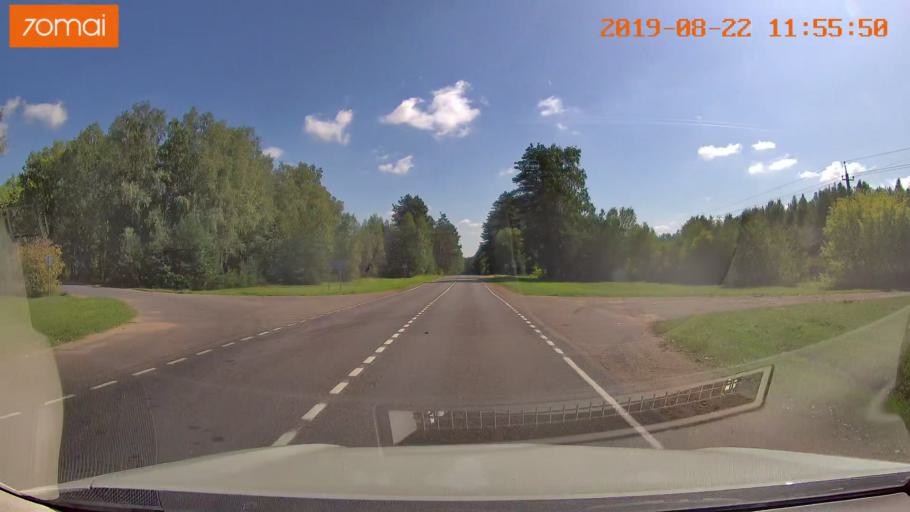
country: BY
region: Minsk
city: Prawdzinski
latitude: 53.4302
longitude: 27.5569
